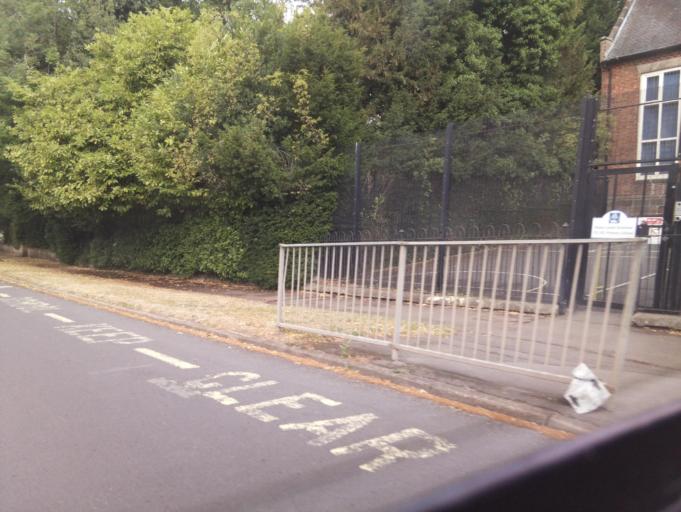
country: GB
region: England
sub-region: Derbyshire
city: Long Eaton
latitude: 52.9166
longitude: -1.3144
